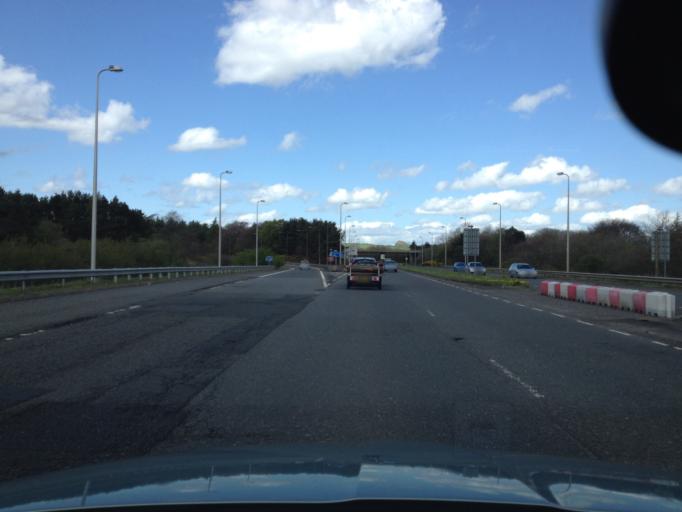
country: GB
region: Scotland
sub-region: West Lothian
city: Livingston
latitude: 55.9168
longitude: -3.5253
